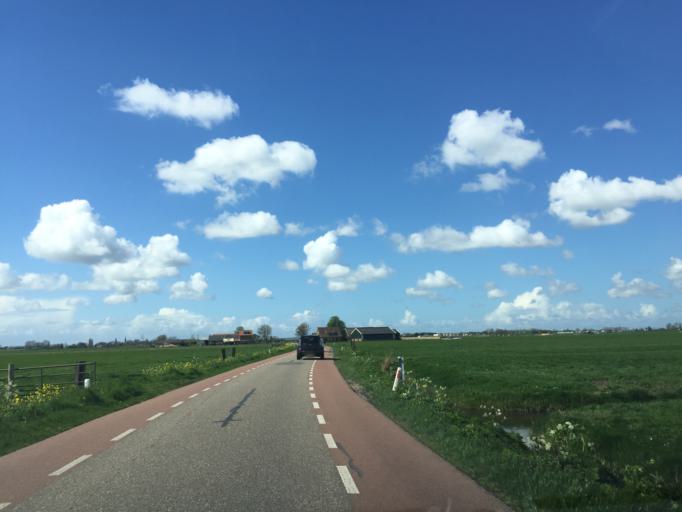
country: NL
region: South Holland
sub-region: Gemeente Kaag en Braassem
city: Leimuiden
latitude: 52.2073
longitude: 4.6997
